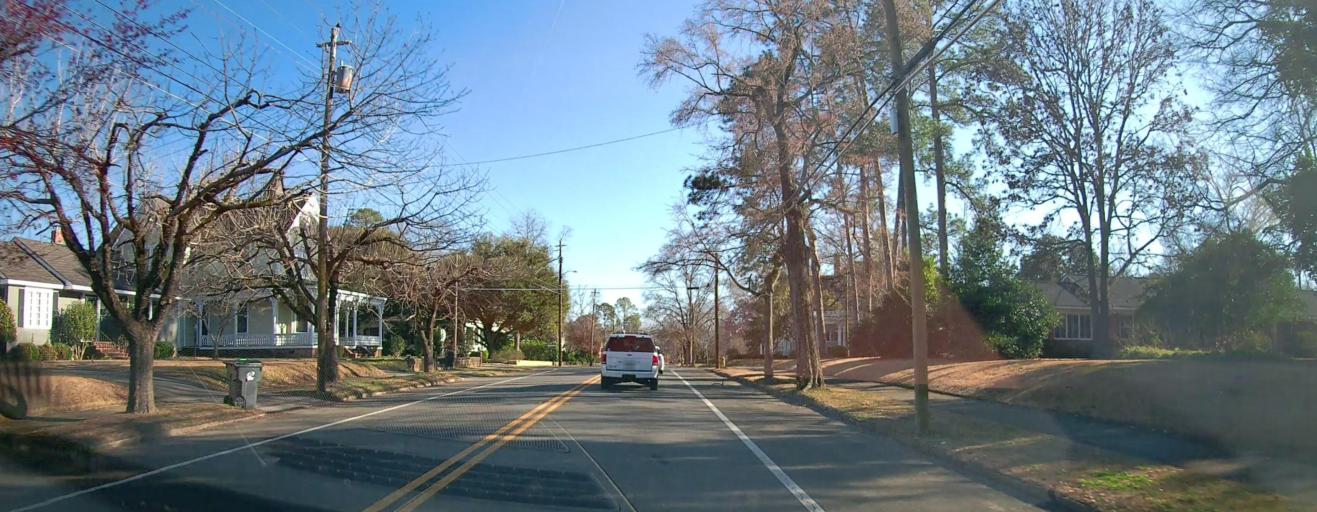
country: US
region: Georgia
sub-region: Sumter County
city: Americus
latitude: 32.0646
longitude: -84.2297
